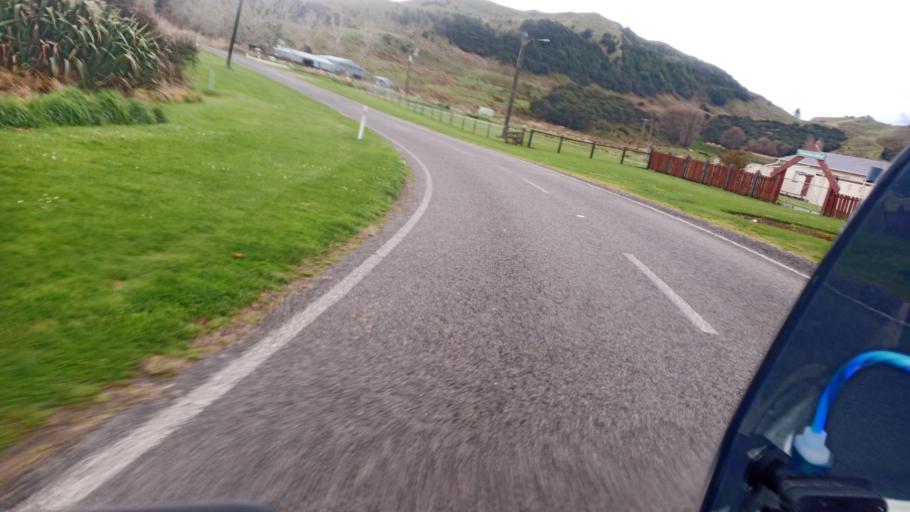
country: NZ
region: Gisborne
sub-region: Gisborne District
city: Gisborne
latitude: -38.3474
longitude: 178.3026
